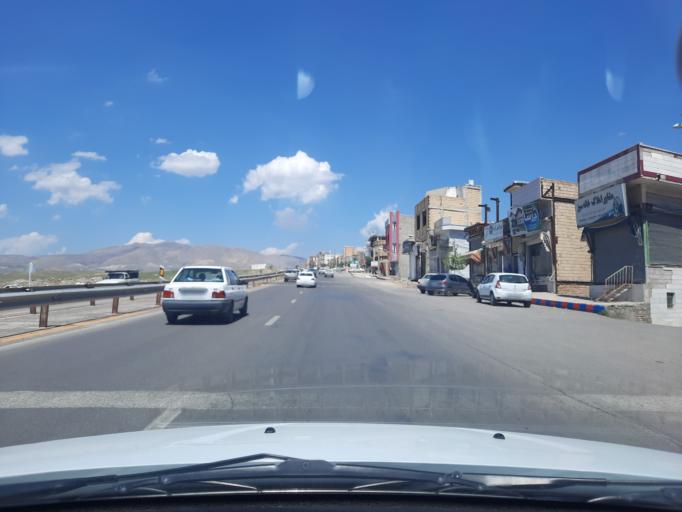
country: IR
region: Qazvin
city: Alvand
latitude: 36.2865
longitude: 50.1320
